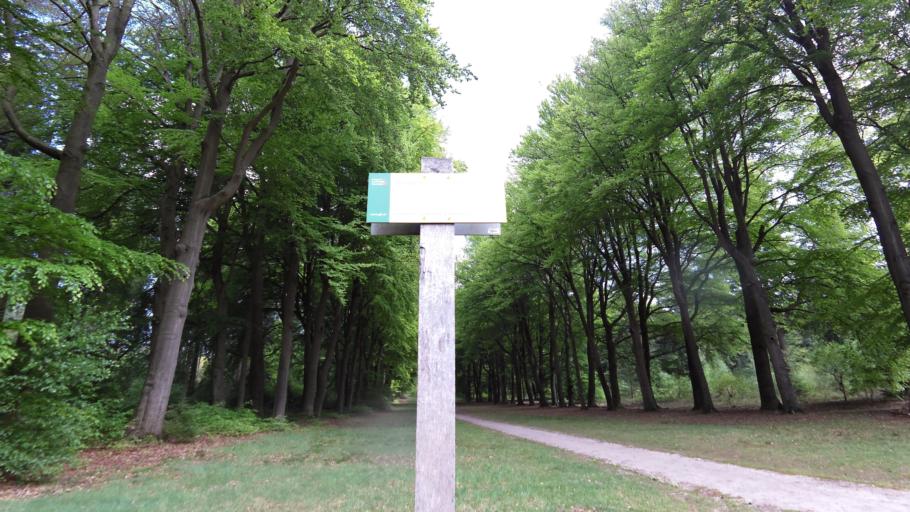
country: NL
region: Gelderland
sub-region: Gemeente Ede
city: Bennekom
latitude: 52.0161
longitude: 5.6842
